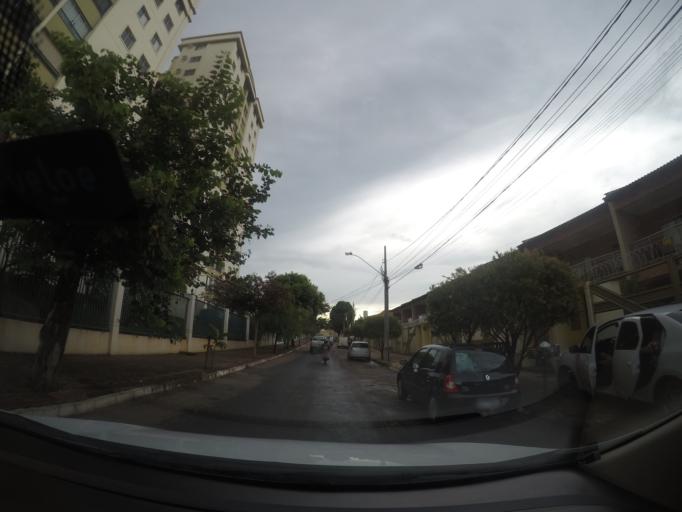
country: BR
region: Goias
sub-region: Goiania
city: Goiania
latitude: -16.6886
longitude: -49.3013
